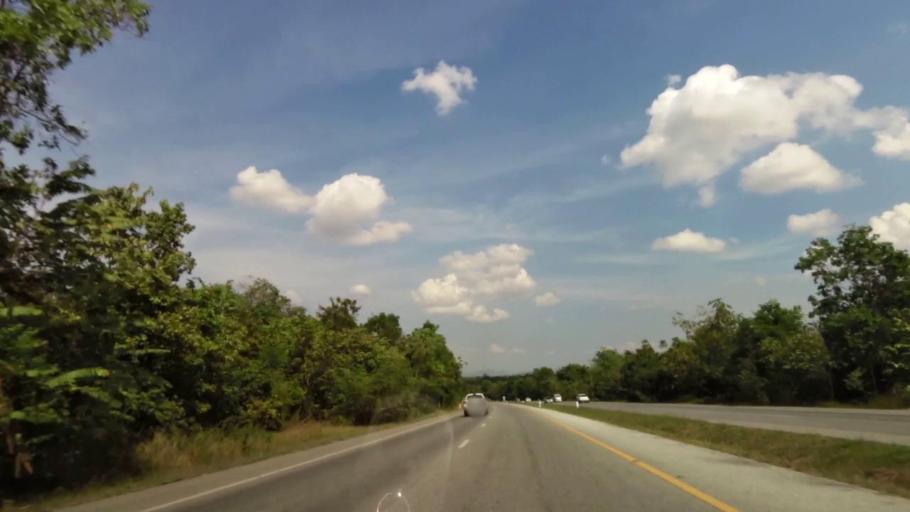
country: TH
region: Uttaradit
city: Thong Saen Khan
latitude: 17.4548
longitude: 100.2375
